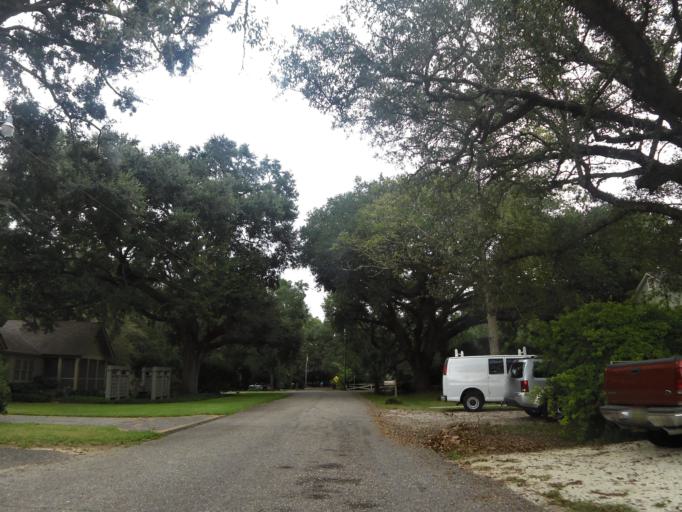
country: US
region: Alabama
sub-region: Baldwin County
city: Fairhope
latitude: 30.5172
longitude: -87.9026
